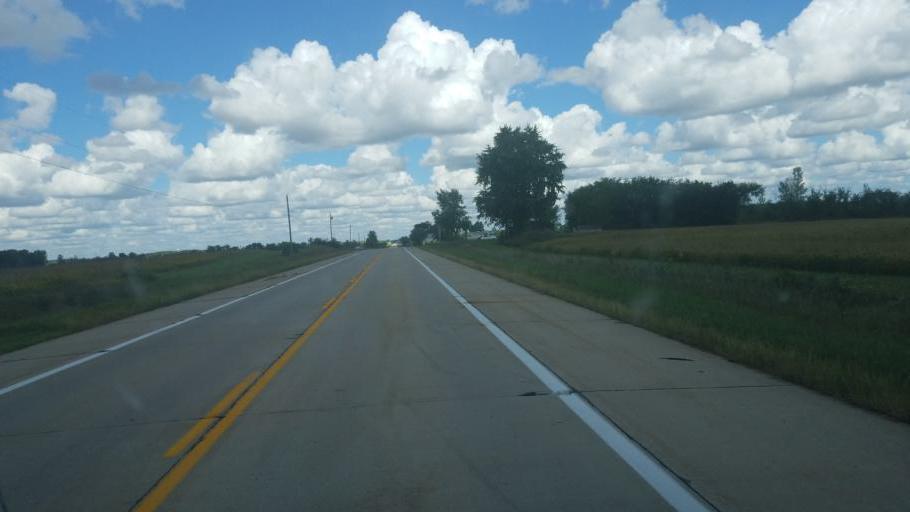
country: US
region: Ohio
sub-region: Champaign County
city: North Lewisburg
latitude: 40.3149
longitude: -83.4977
